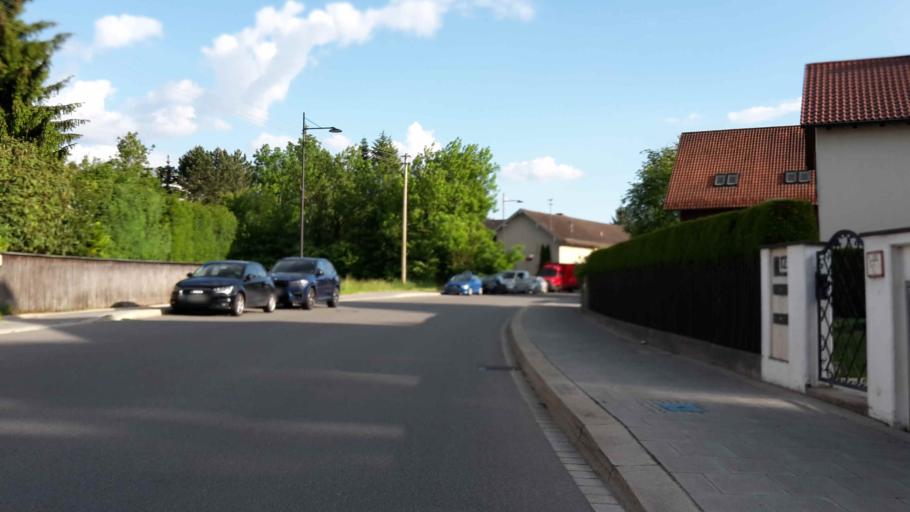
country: DE
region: Bavaria
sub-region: Upper Bavaria
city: Unterfoehring
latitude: 48.1991
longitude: 11.6477
